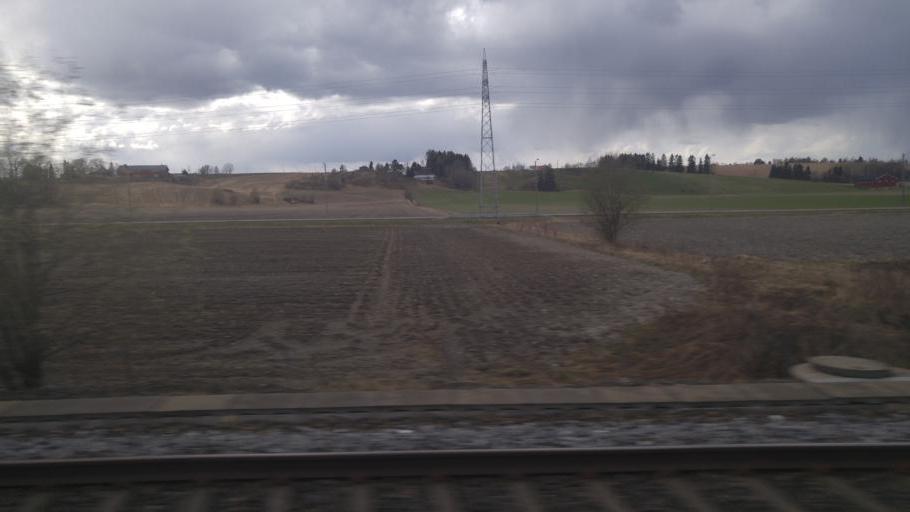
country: NO
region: Akershus
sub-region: Skedsmo
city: Leirsund
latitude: 59.9764
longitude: 11.0707
